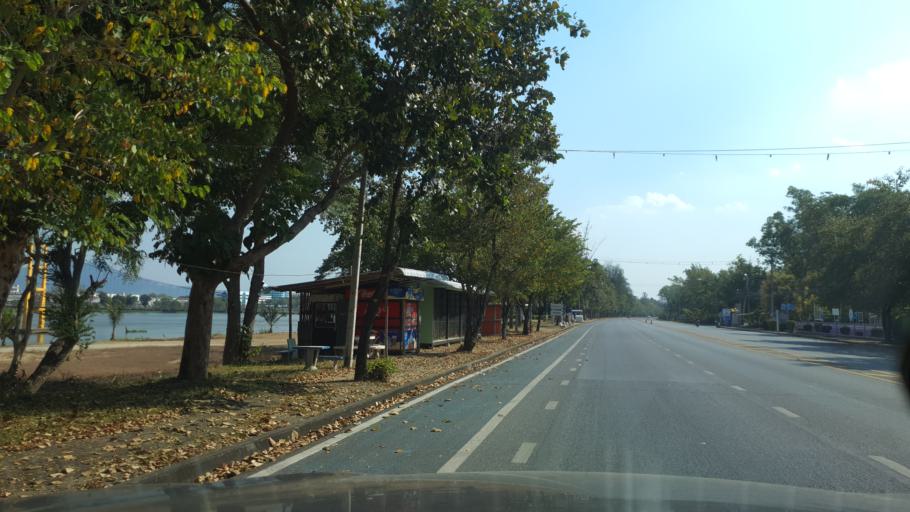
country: TH
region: Tak
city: Tak
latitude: 16.8777
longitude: 99.1160
